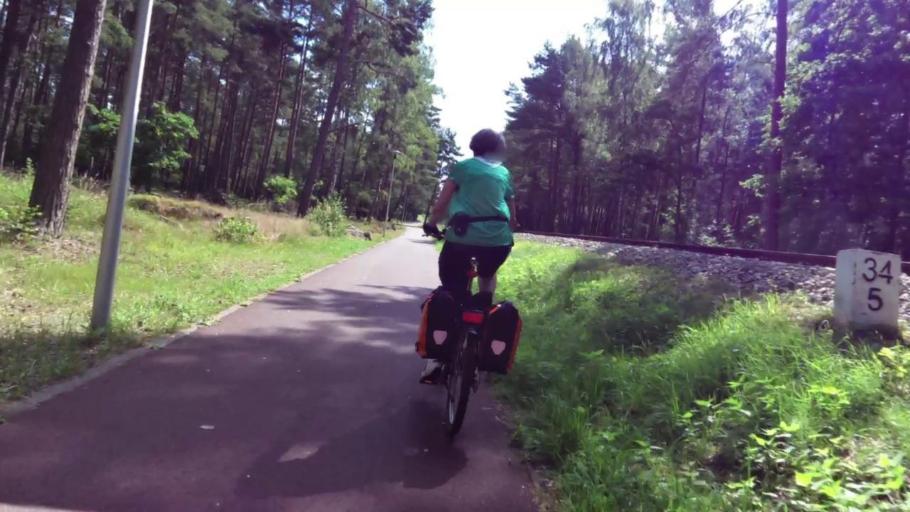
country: PL
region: West Pomeranian Voivodeship
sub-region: Powiat gryficki
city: Karnice
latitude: 54.0943
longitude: 15.1112
